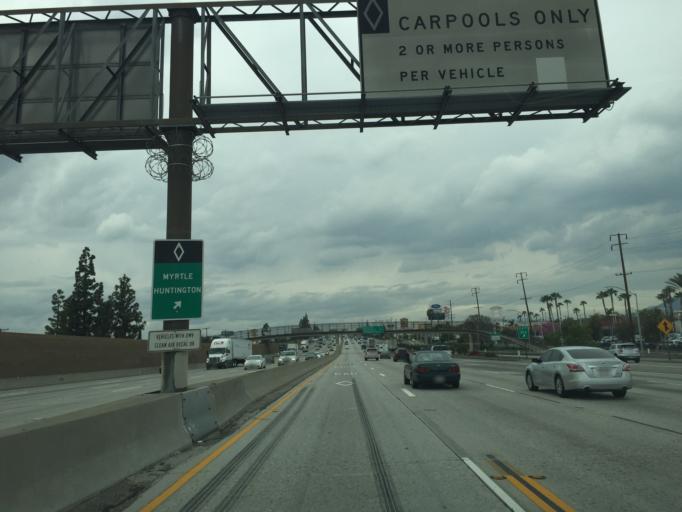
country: US
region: California
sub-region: Los Angeles County
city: Duarte
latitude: 34.1354
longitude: -117.9786
